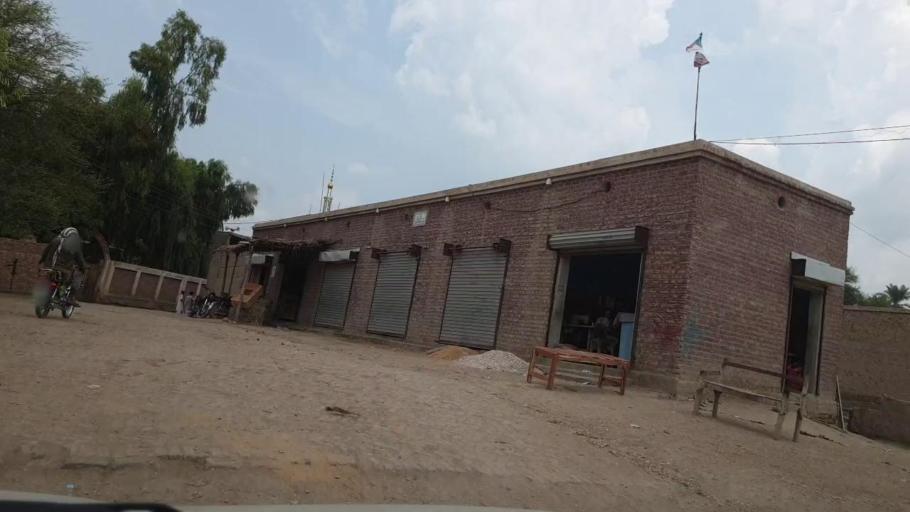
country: PK
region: Sindh
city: Dokri
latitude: 27.3989
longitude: 68.1125
